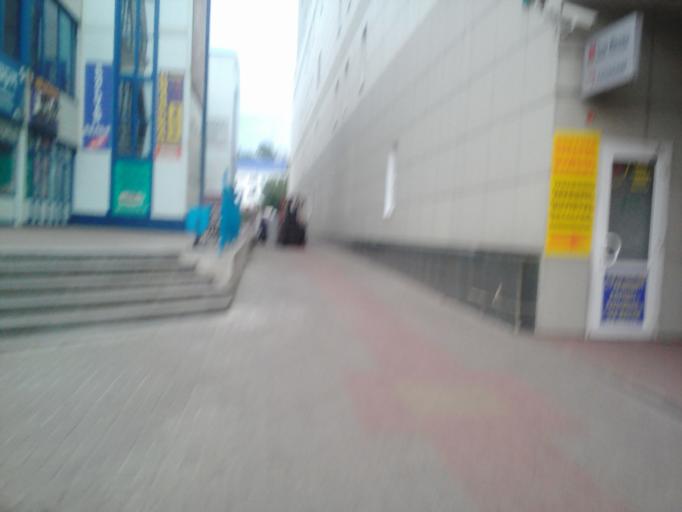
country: RU
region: Kursk
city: Kursk
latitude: 51.7278
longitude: 36.1842
